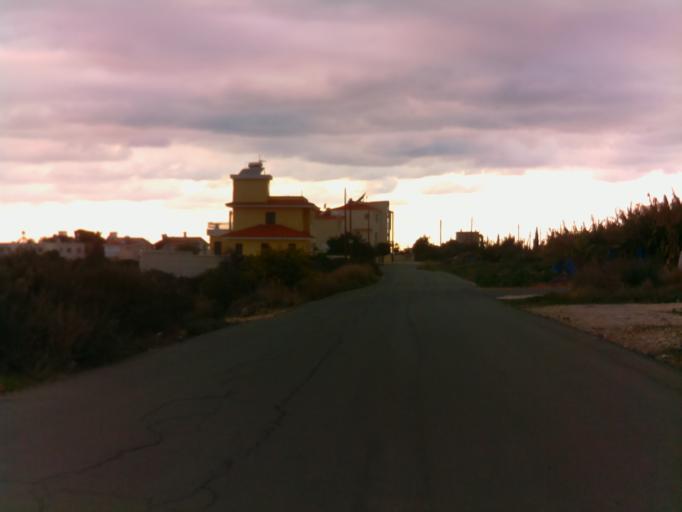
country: CY
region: Pafos
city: Pegeia
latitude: 34.8849
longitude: 32.3402
